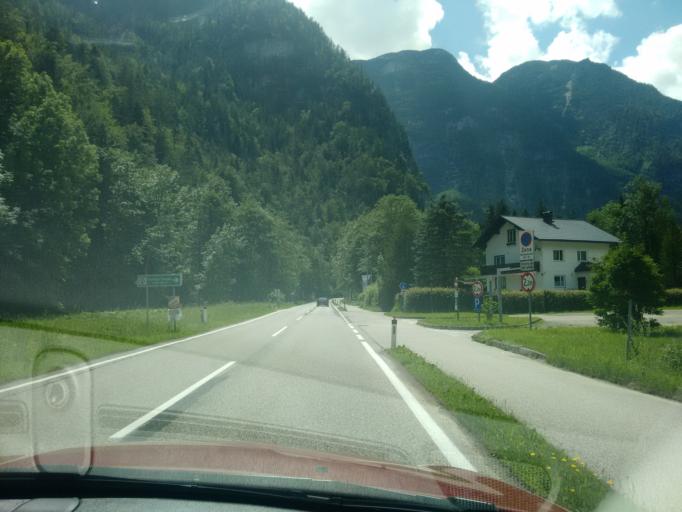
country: AT
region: Upper Austria
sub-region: Politischer Bezirk Gmunden
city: Bad Goisern
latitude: 47.5492
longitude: 13.6783
